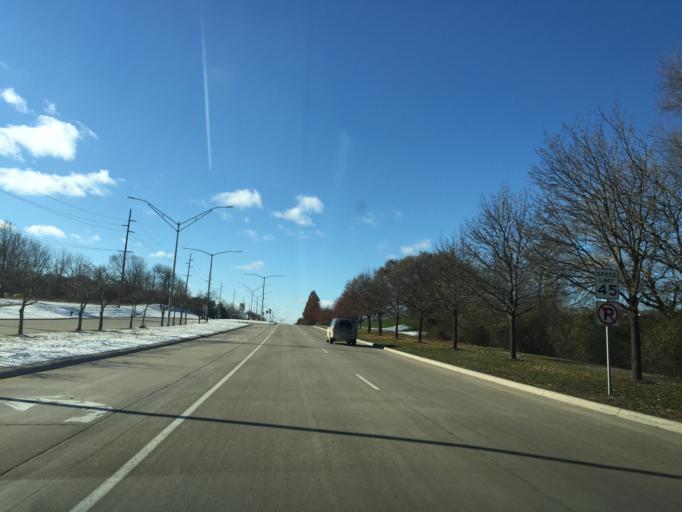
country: US
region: Michigan
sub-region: Oakland County
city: Auburn Hills
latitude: 42.6498
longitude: -83.2246
